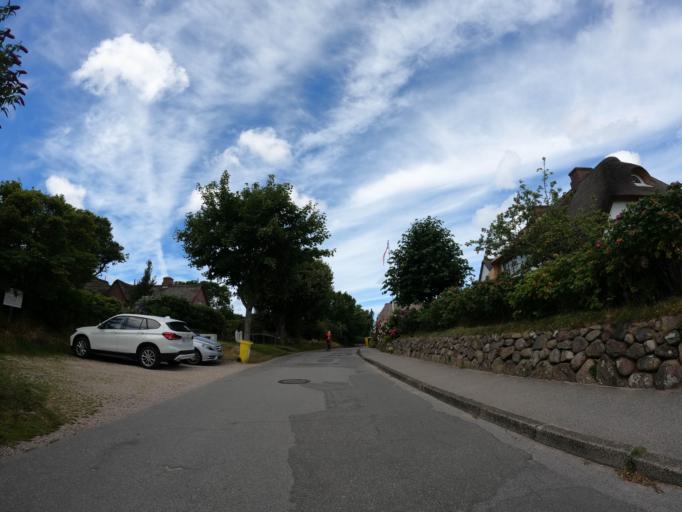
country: DE
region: Schleswig-Holstein
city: Keitum
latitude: 54.8994
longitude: 8.3684
